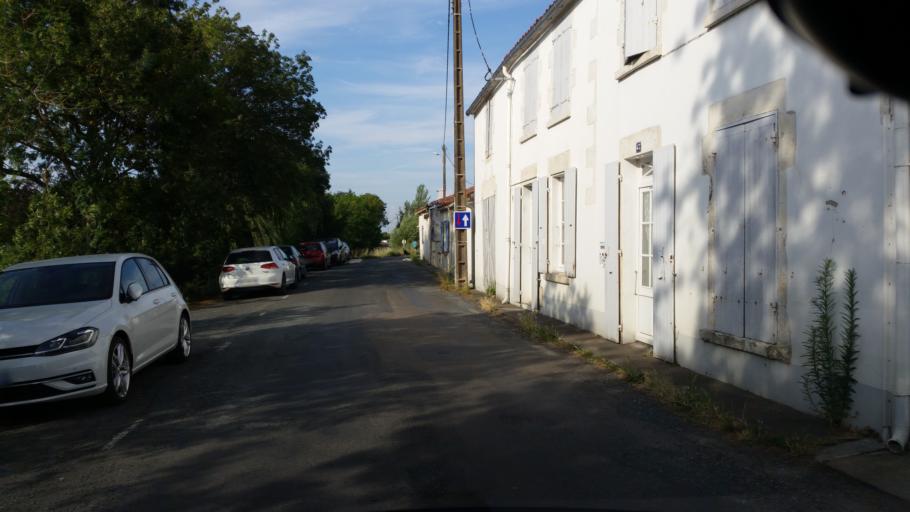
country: FR
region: Poitou-Charentes
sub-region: Departement de la Charente-Maritime
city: Marans
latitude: 46.3122
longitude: -0.9883
